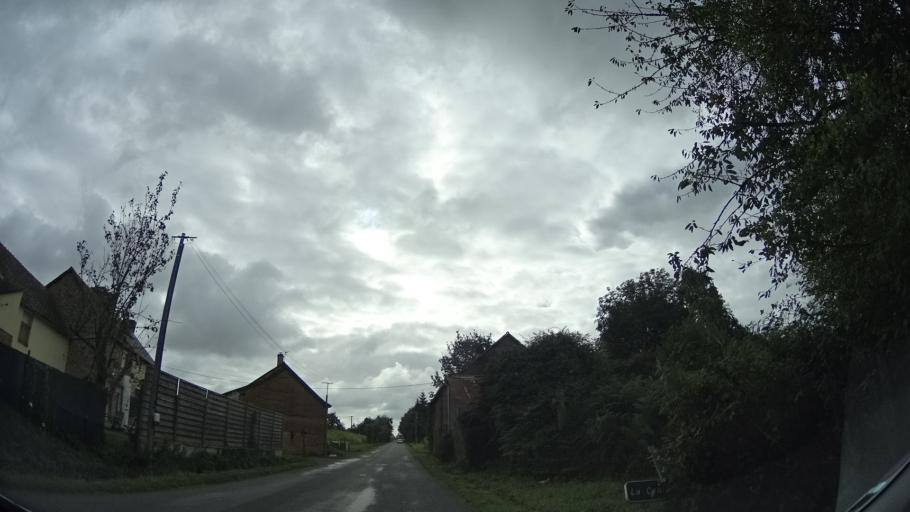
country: FR
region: Brittany
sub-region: Departement d'Ille-et-Vilaine
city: Montreuil-sur-Ille
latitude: 48.3019
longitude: -1.6556
